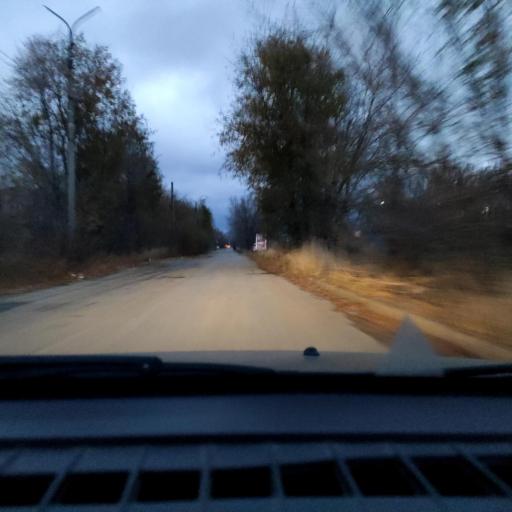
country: RU
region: Samara
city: Tol'yatti
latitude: 53.5609
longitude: 49.3117
